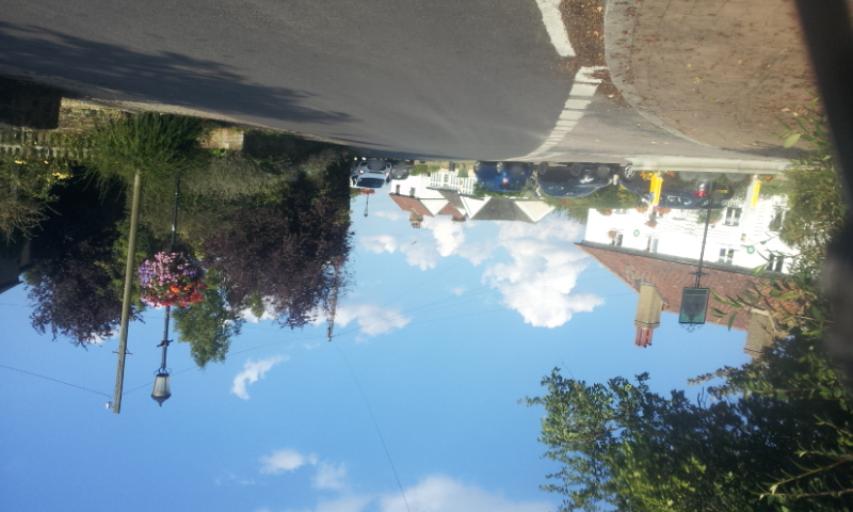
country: GB
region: England
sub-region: Kent
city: Swanley
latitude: 51.4050
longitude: 0.1925
